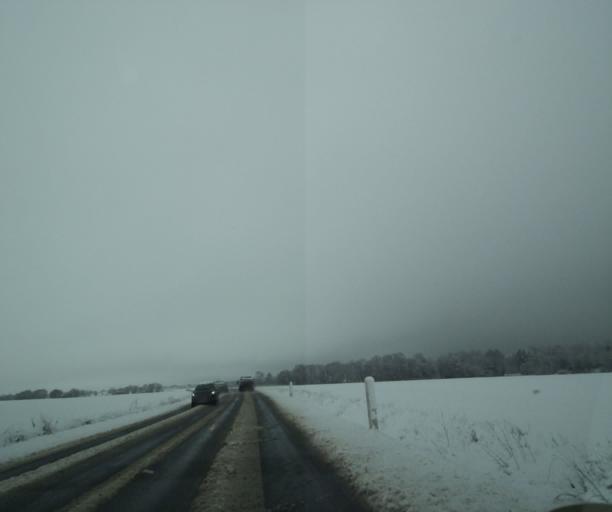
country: FR
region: Champagne-Ardenne
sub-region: Departement de la Haute-Marne
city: Wassy
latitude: 48.5651
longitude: 4.9219
